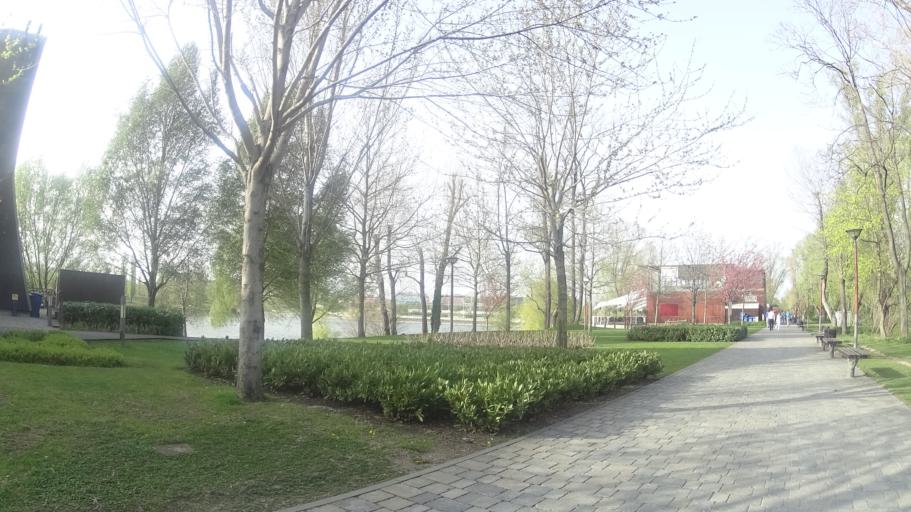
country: HU
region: Budapest
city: Budapest IX. keruelet
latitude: 47.4632
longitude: 19.0617
